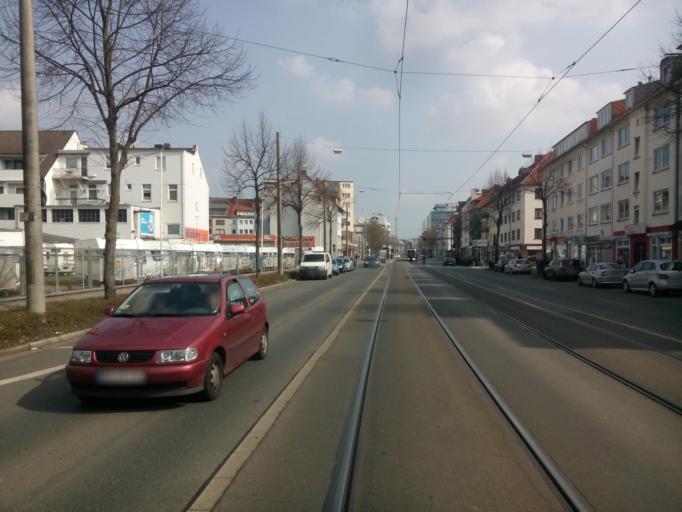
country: DE
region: Bremen
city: Bremen
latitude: 53.0732
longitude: 8.7920
